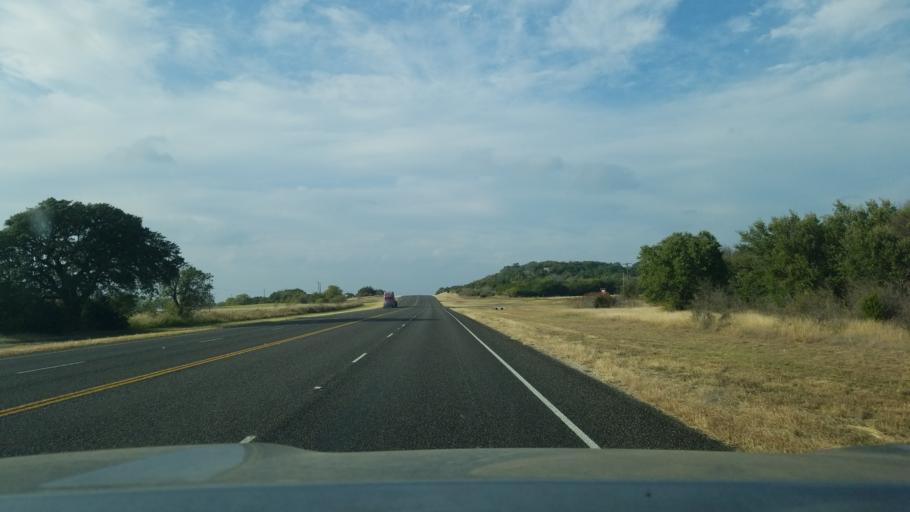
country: US
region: Texas
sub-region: Mills County
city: Goldthwaite
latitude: 31.2549
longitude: -98.4331
